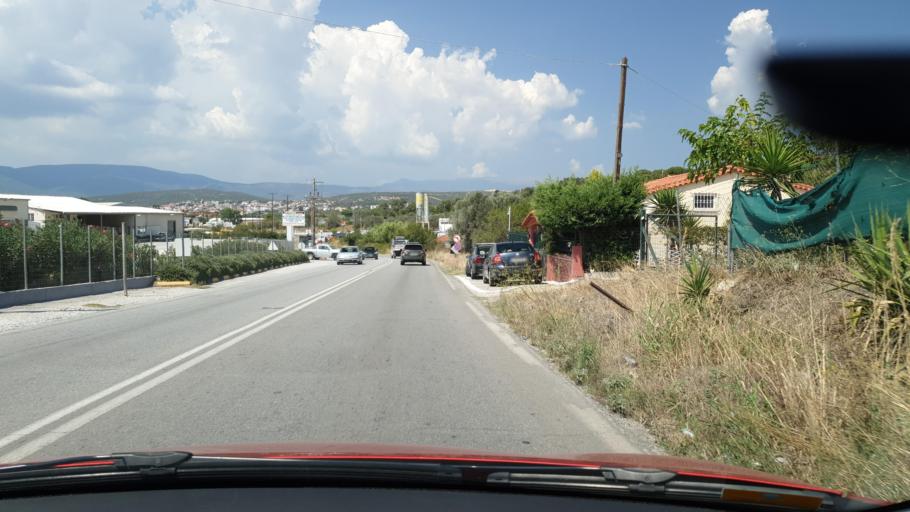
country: GR
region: Central Greece
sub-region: Nomos Evvoias
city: Aliveri
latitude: 38.3979
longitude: 24.0626
